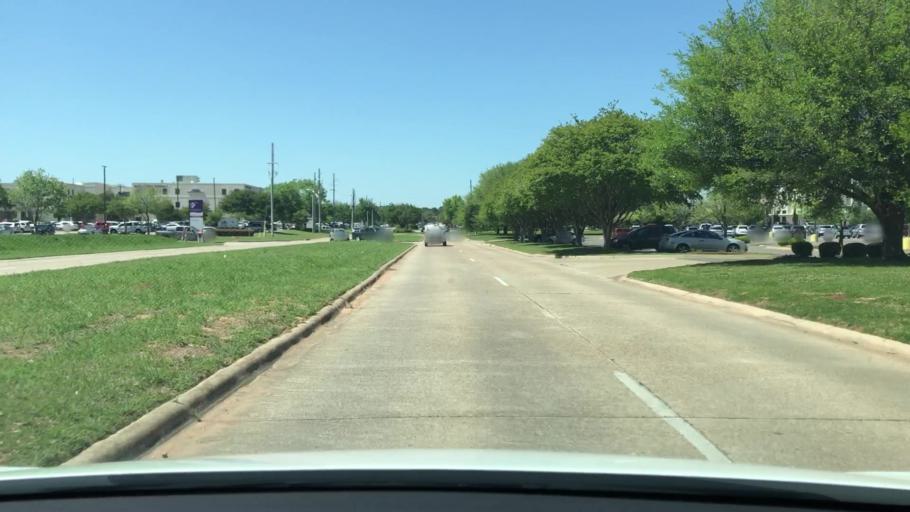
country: US
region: Louisiana
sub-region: Bossier Parish
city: Bossier City
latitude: 32.4252
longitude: -93.7139
